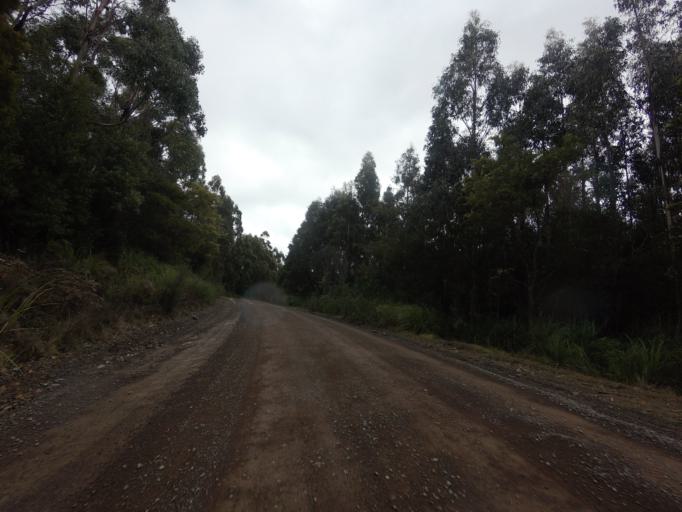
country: AU
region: Tasmania
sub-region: Huon Valley
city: Geeveston
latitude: -43.4720
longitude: 146.8921
